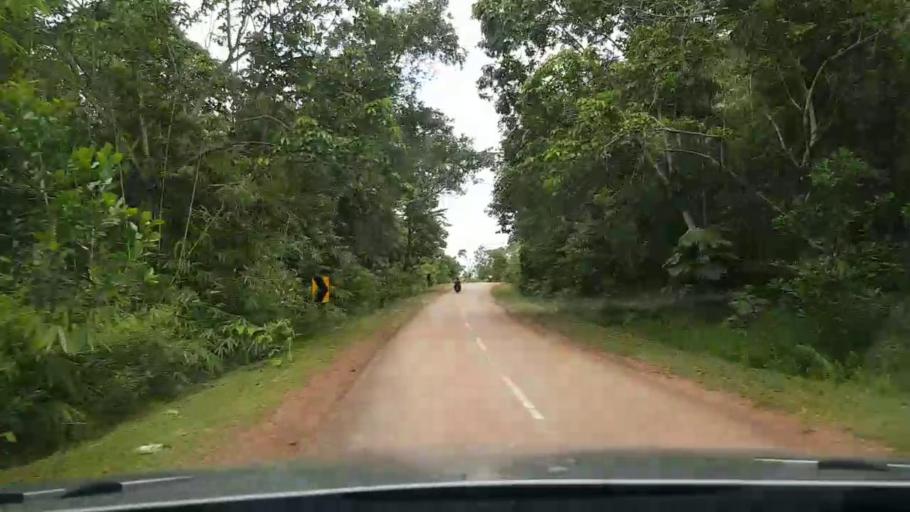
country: MY
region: Pahang
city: Pekan
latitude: 3.1398
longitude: 102.9725
